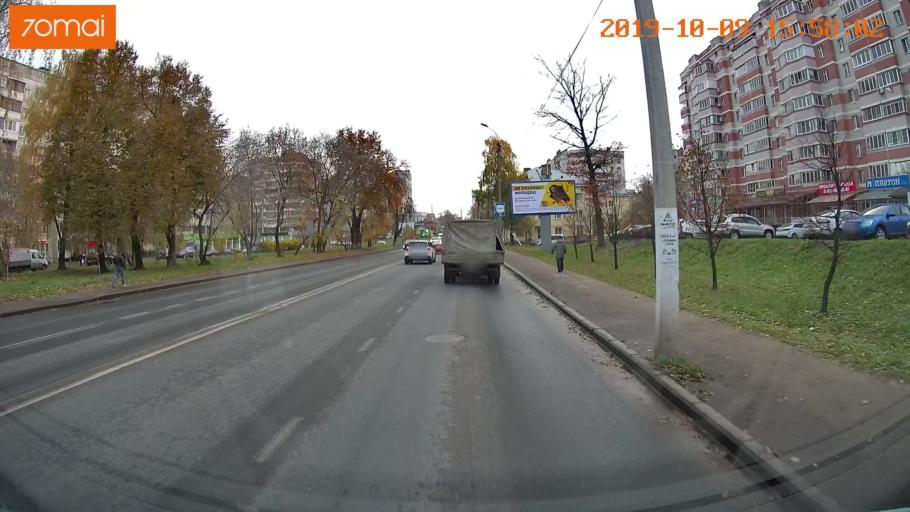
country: RU
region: Kostroma
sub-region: Kostromskoy Rayon
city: Kostroma
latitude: 57.7683
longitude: 40.9508
